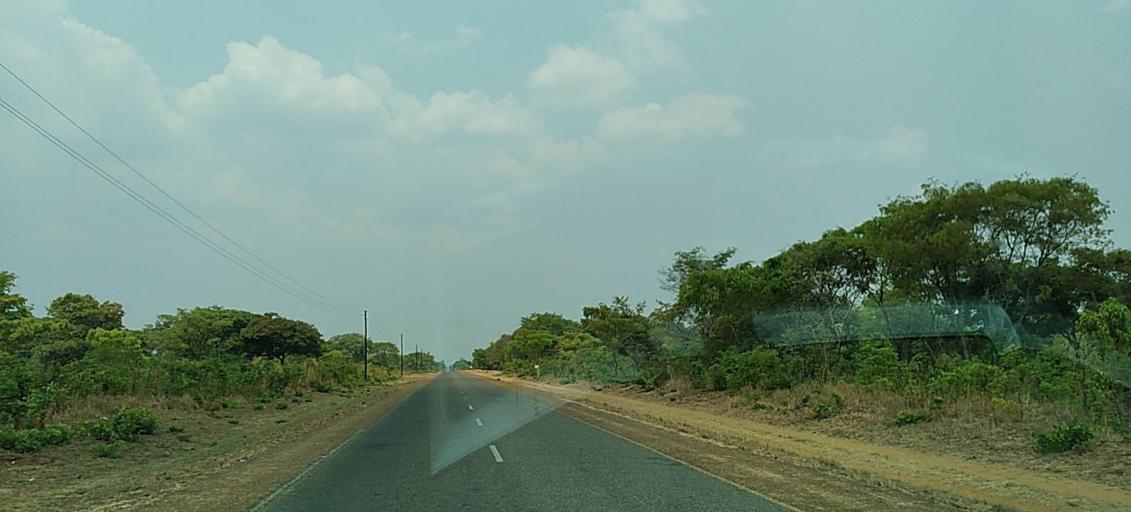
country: ZM
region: North-Western
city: Zambezi
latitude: -13.5527
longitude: 23.1437
